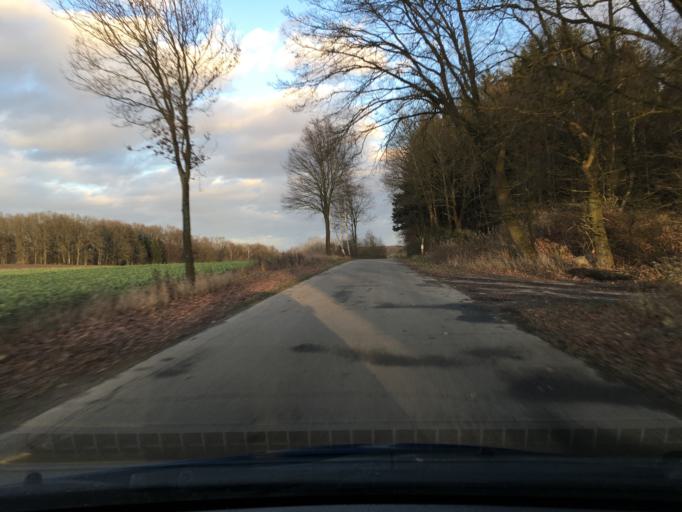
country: DE
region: Lower Saxony
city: Amelinghausen
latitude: 53.1350
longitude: 10.1836
